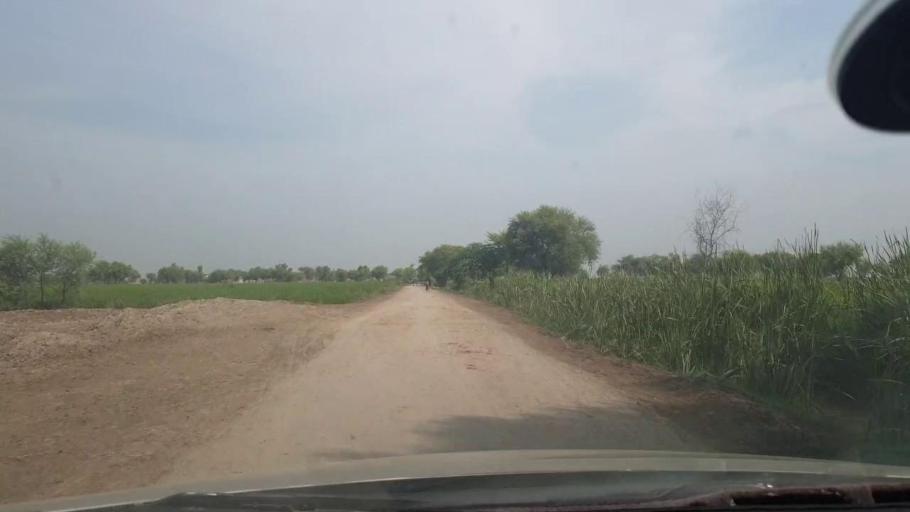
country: PK
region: Sindh
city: Jacobabad
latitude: 28.2929
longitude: 68.4802
